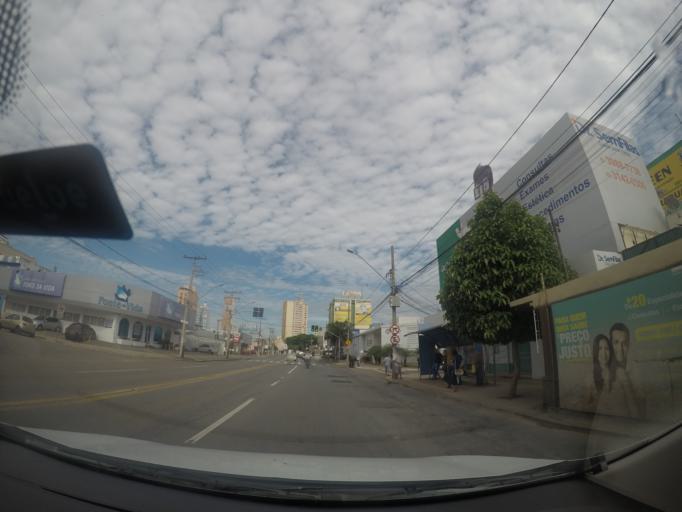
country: BR
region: Goias
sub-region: Goiania
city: Goiania
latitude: -16.6704
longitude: -49.2554
